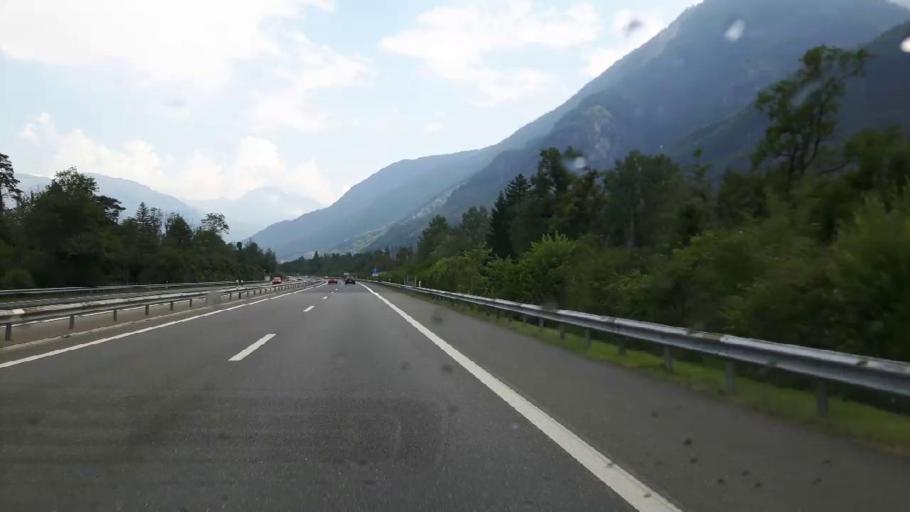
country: CH
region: Ticino
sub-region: Riviera District
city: Lodrino
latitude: 46.2825
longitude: 8.9934
